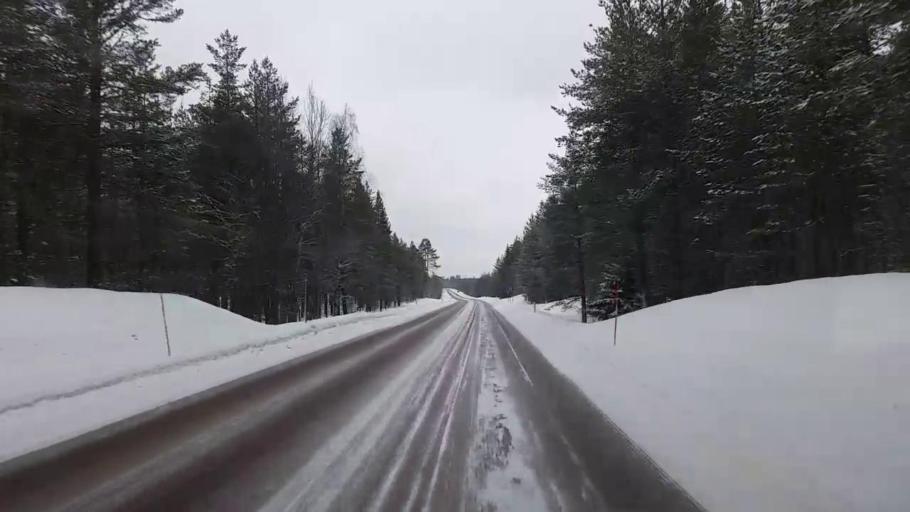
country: SE
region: Jaemtland
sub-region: Bergs Kommun
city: Hoverberg
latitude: 62.4483
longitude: 14.5647
